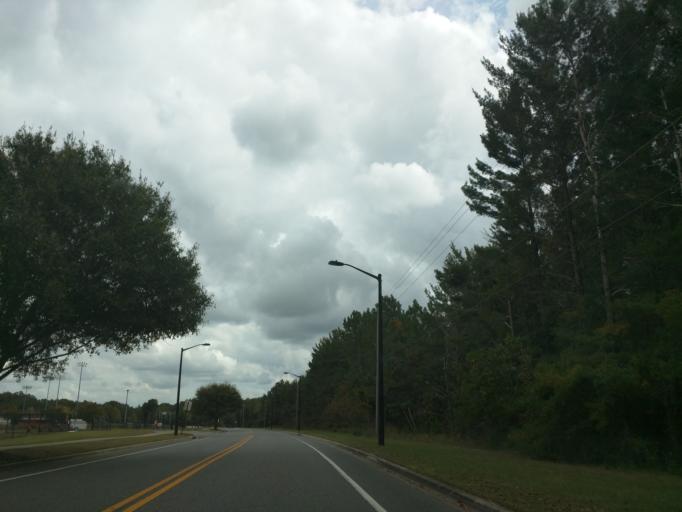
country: US
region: Florida
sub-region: Leon County
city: Woodville
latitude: 30.3824
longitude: -84.2241
